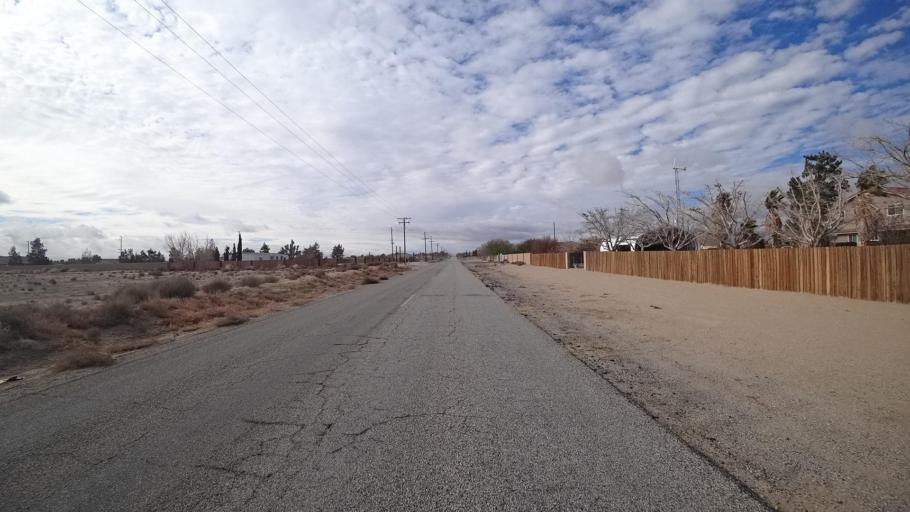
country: US
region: California
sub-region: Kern County
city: Rosamond
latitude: 34.8201
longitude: -118.2535
